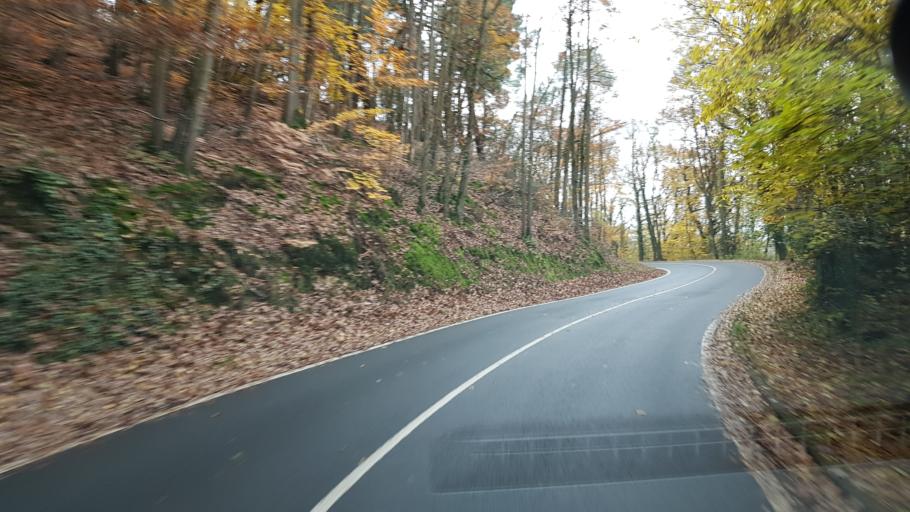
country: FR
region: Ile-de-France
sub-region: Departement des Yvelines
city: Dampierre-en-Yvelines
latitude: 48.7103
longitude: 1.9955
